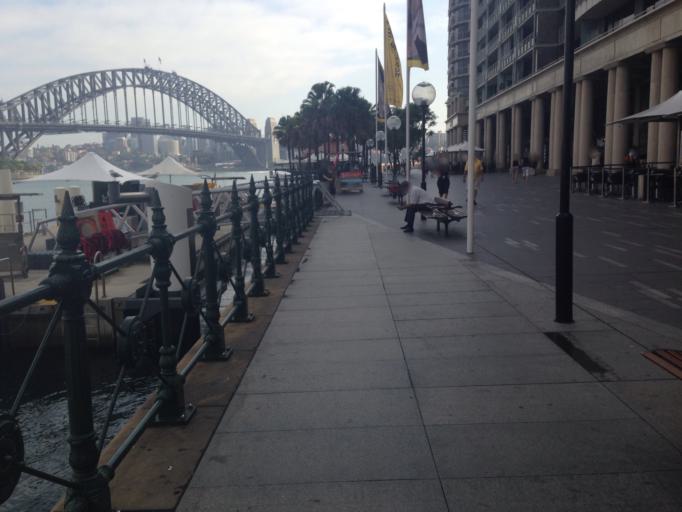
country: AU
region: New South Wales
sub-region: City of Sydney
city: Sydney
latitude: -33.8604
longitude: 151.2127
